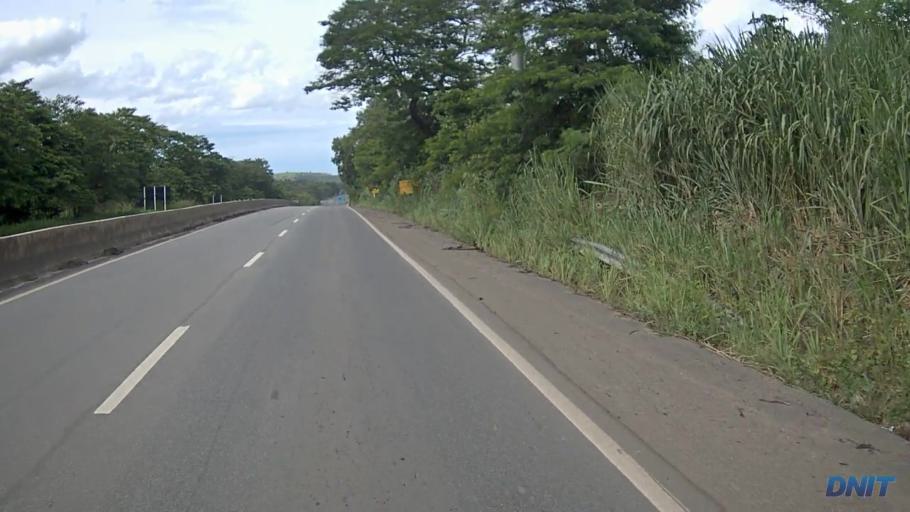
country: BR
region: Minas Gerais
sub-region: Ipaba
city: Ipaba
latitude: -19.3196
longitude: -42.4041
